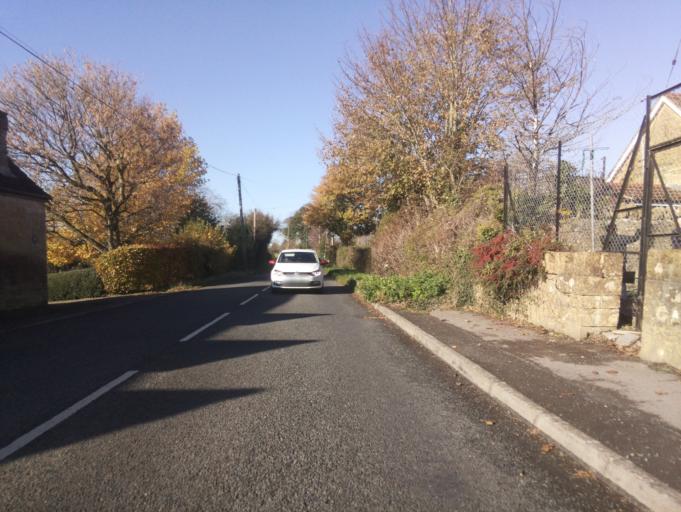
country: GB
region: England
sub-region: Somerset
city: Ilchester
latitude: 50.9652
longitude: -2.6797
